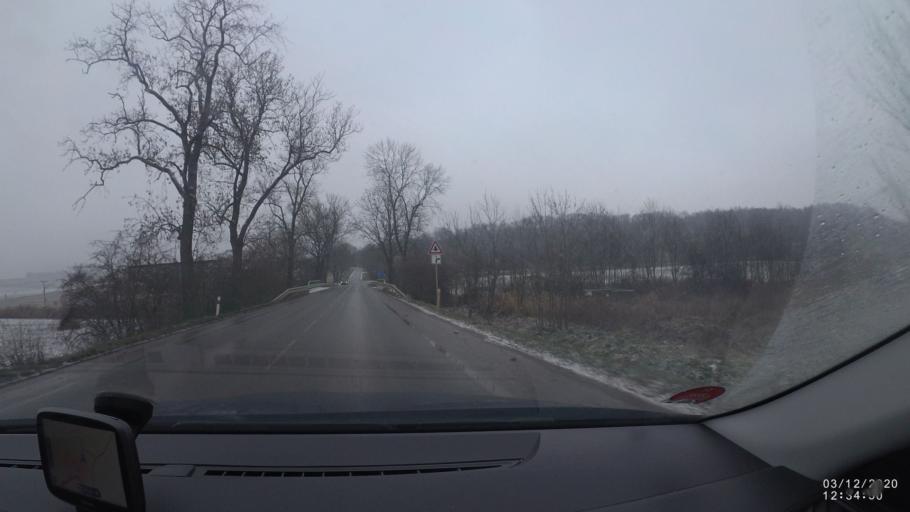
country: CZ
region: Central Bohemia
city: Revnicov
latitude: 50.1888
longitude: 13.8123
